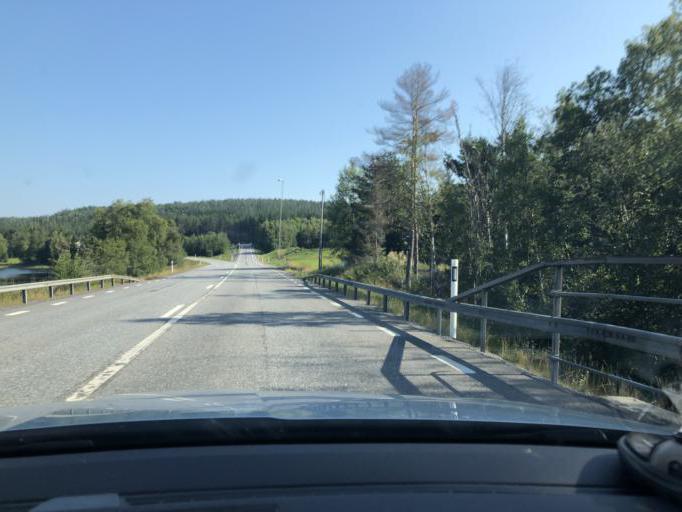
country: SE
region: Vaesternorrland
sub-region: Kramfors Kommun
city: Nordingra
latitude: 62.9323
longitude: 18.0892
